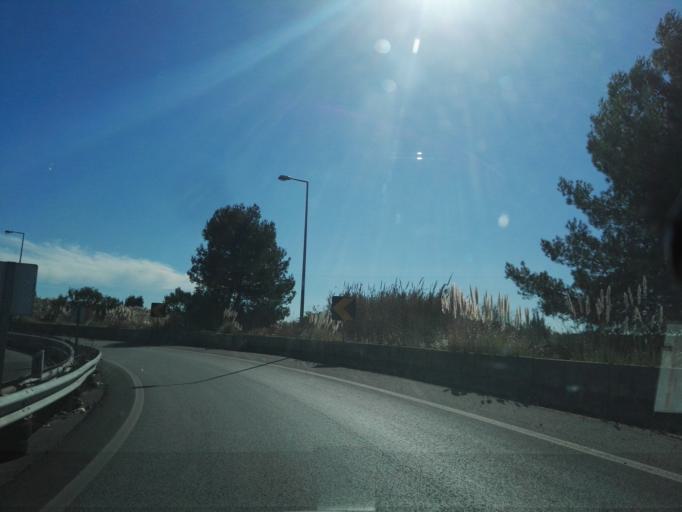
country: PT
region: Lisbon
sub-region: Sintra
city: Rio de Mouro
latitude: 38.7762
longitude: -9.3235
